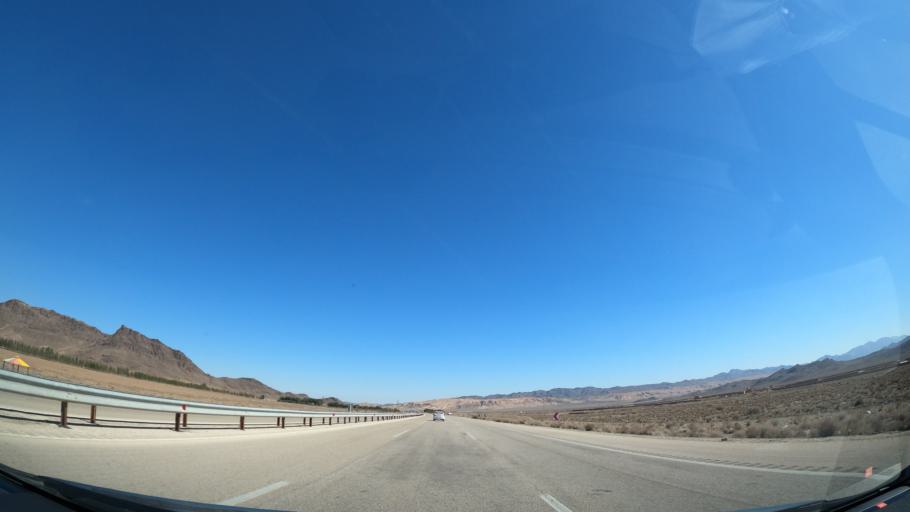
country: IR
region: Isfahan
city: Natanz
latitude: 33.3948
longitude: 51.9673
